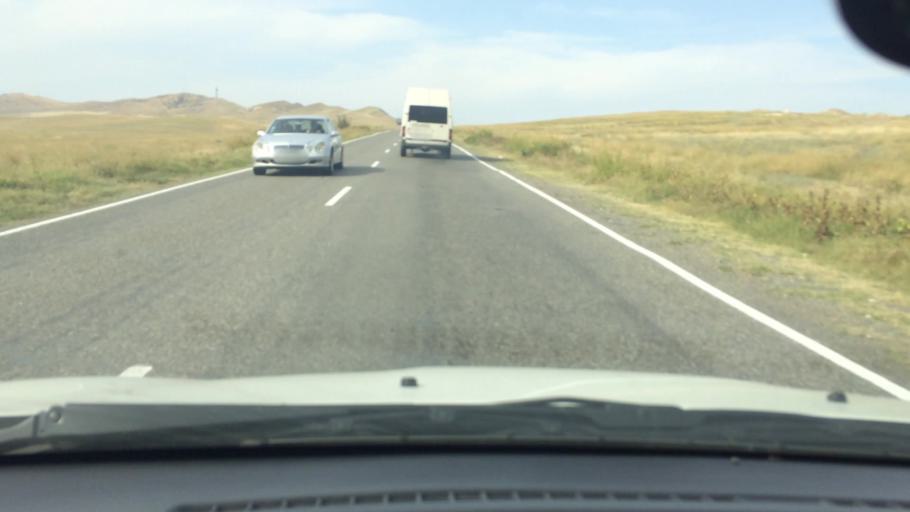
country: GE
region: Kvemo Kartli
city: Rust'avi
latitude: 41.5263
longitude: 44.9813
